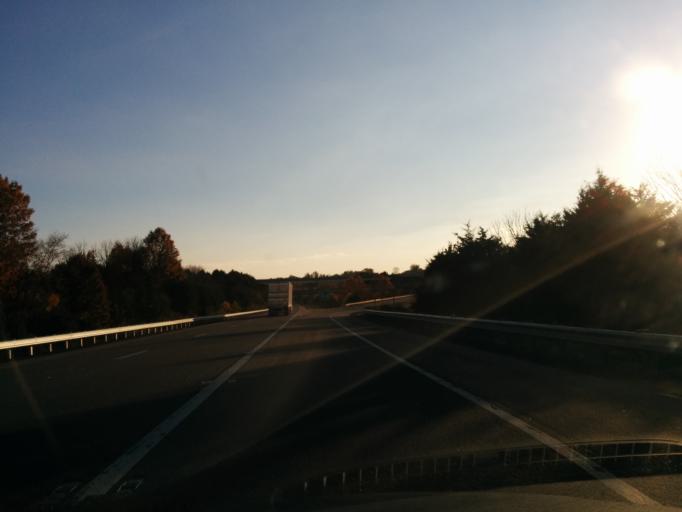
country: US
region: Virginia
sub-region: Rockbridge County
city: East Lexington
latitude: 37.7976
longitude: -79.3957
